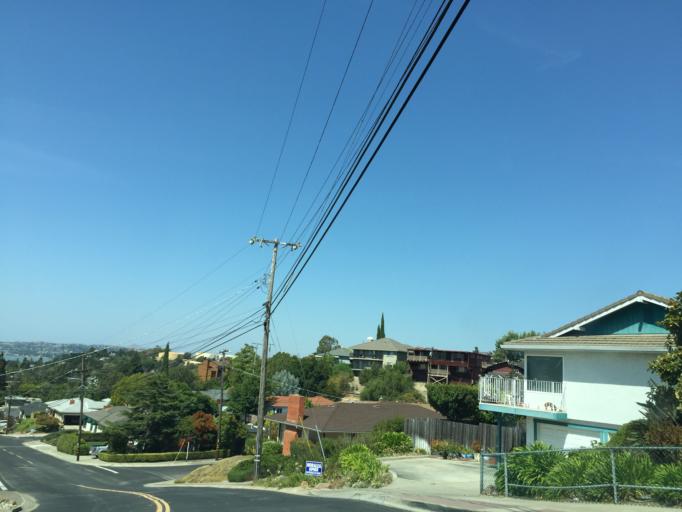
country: US
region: California
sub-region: Contra Costa County
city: Mountain View
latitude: 38.0098
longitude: -122.1252
